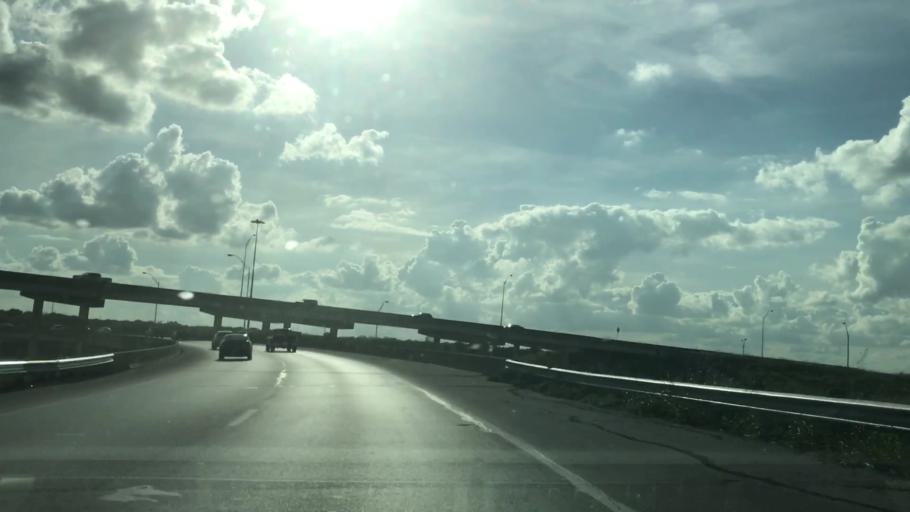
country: US
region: Texas
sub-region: Dallas County
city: Coppell
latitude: 32.9506
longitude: -97.0385
